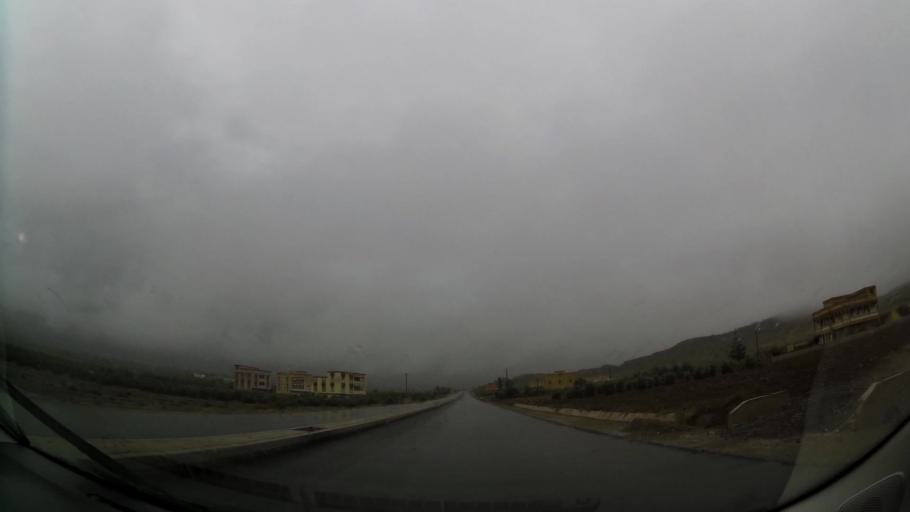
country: MA
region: Oriental
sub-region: Nador
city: Midar
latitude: 34.8383
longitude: -3.7205
